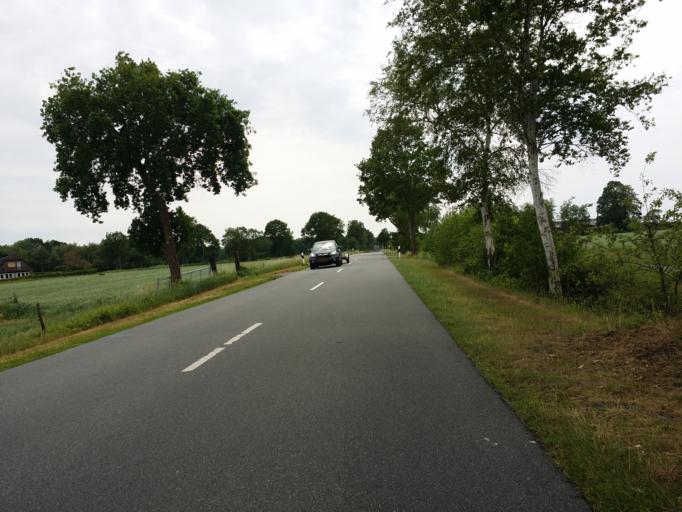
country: DE
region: Lower Saxony
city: Bockhorn
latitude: 53.3278
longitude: 8.0249
